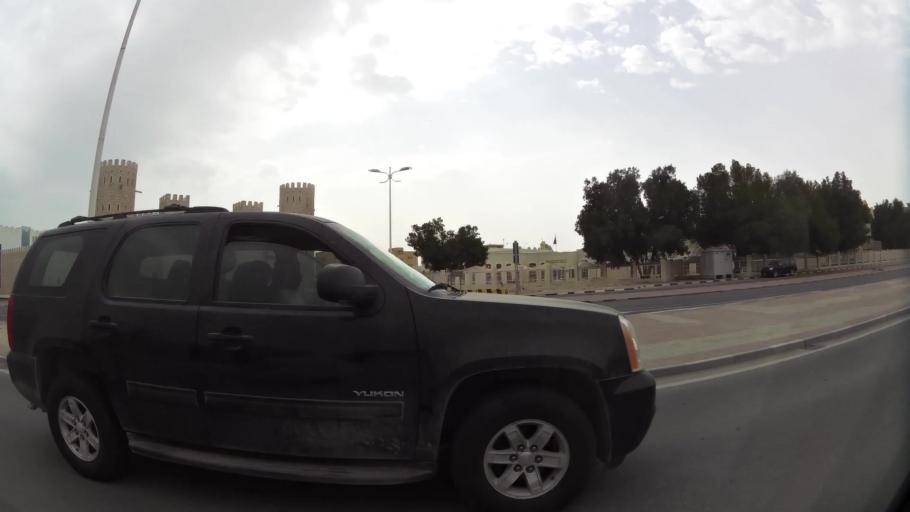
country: QA
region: Baladiyat ad Dawhah
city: Doha
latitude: 25.2984
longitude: 51.4999
